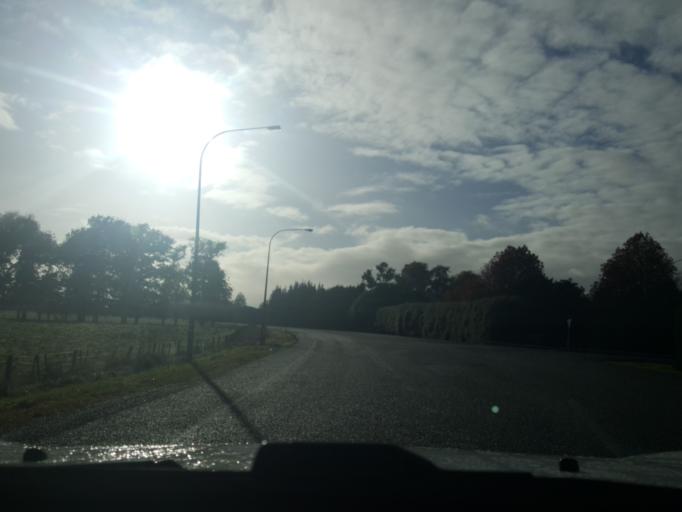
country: NZ
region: Waikato
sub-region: Waipa District
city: Cambridge
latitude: -37.7790
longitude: 175.4005
